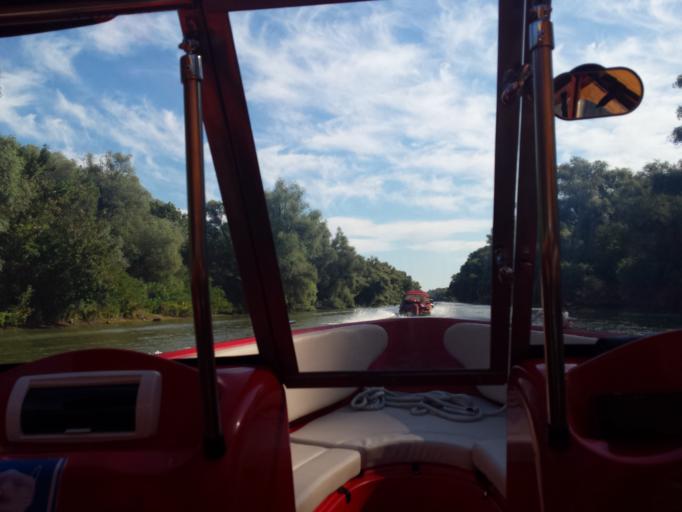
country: RO
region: Tulcea
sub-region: Comuna Nufaru
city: Malcoci
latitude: 45.2156
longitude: 28.8695
